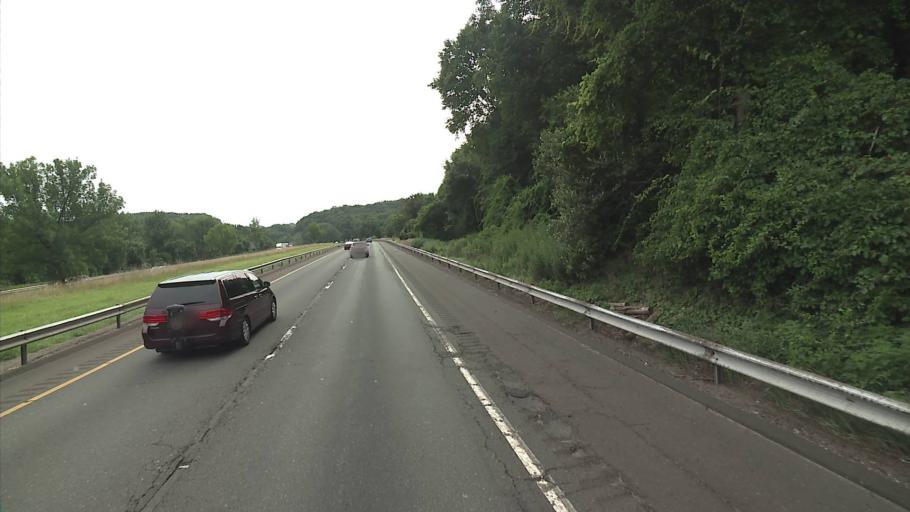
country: US
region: Connecticut
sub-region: Fairfield County
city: Newtown
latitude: 41.4265
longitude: -73.3305
